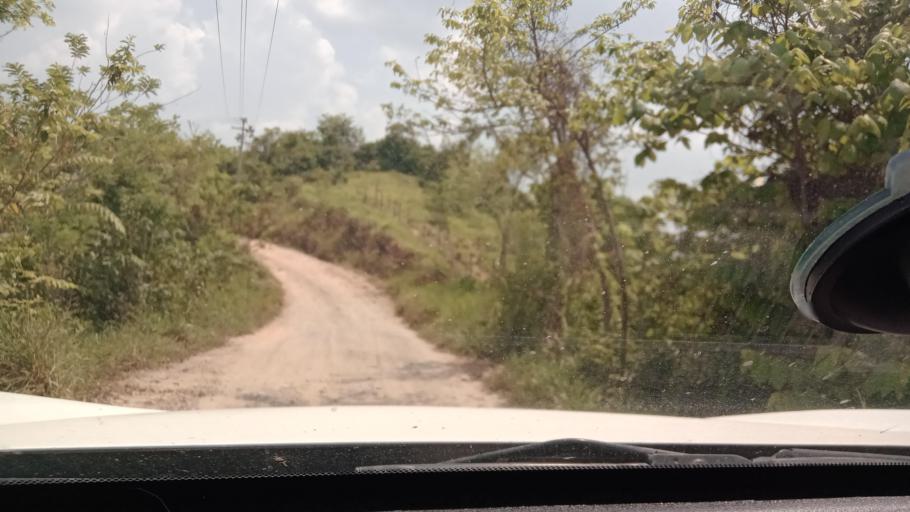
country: MX
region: Tabasco
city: Chontalpa
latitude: 17.5788
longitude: -93.6978
